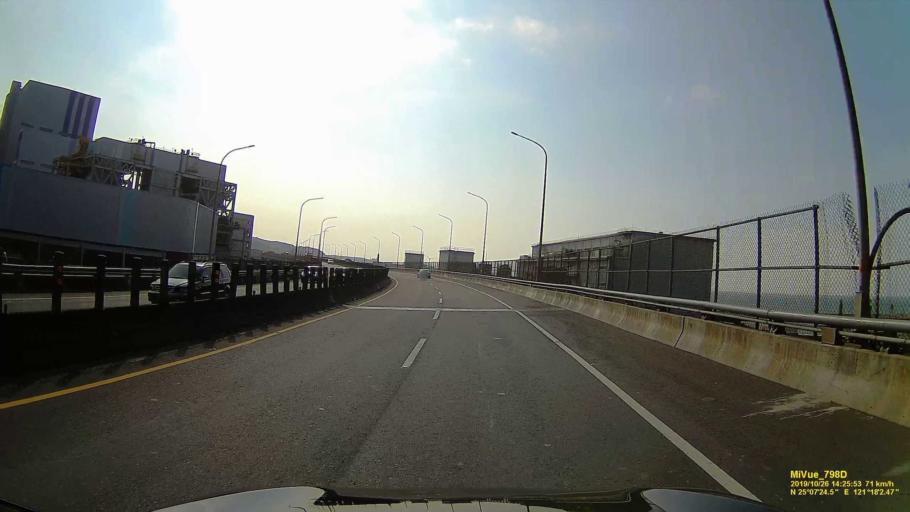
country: TW
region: Taiwan
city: Taoyuan City
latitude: 25.1233
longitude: 121.3021
